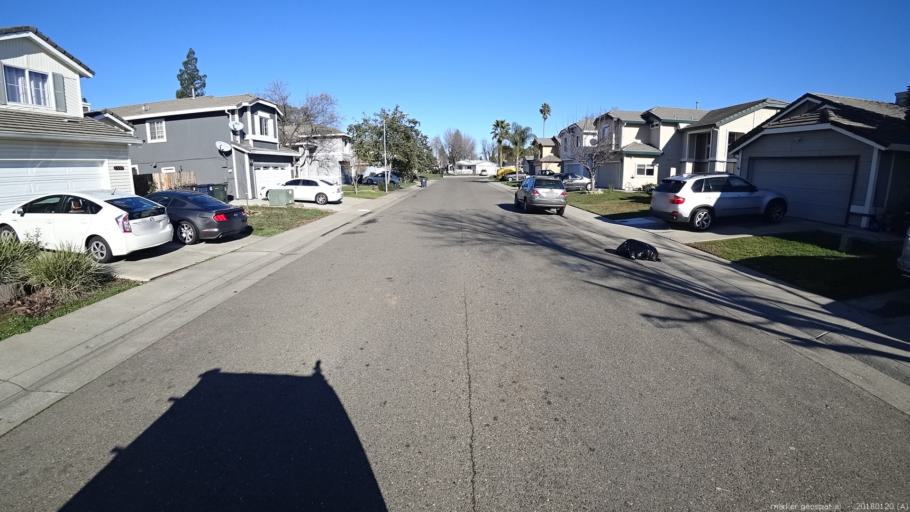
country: US
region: California
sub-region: Sacramento County
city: Rancho Cordova
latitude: 38.5681
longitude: -121.3115
